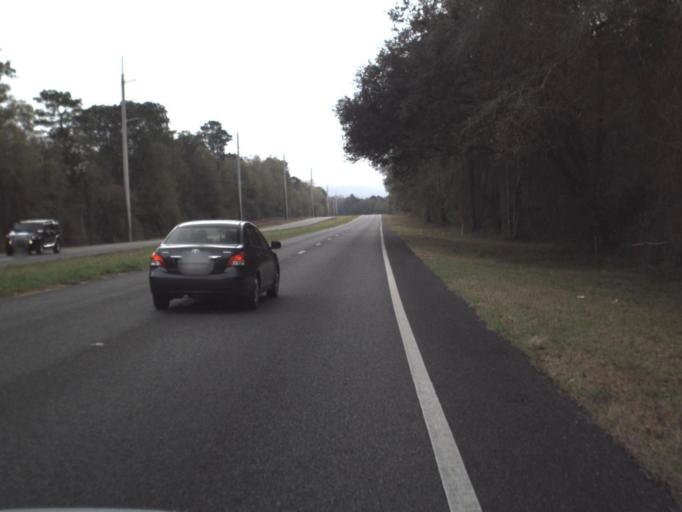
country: US
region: Florida
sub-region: Leon County
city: Woodville
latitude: 30.4178
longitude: -84.0903
